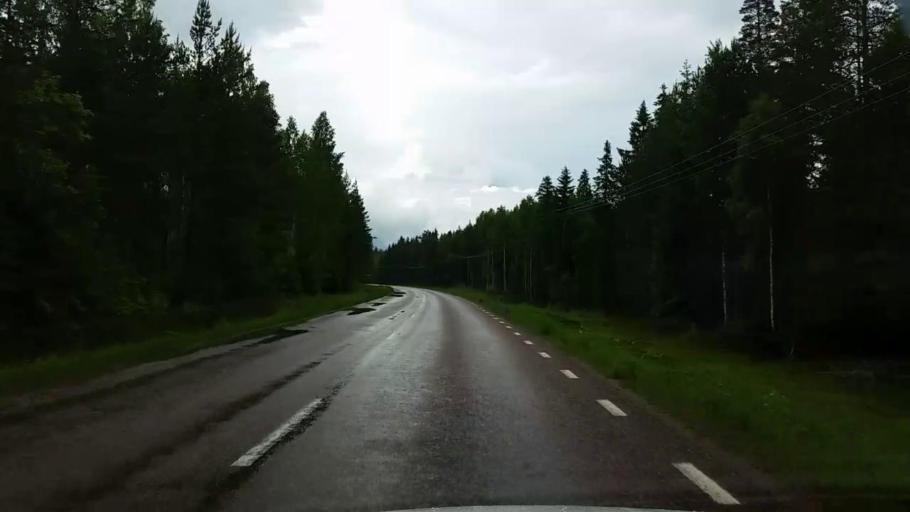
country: SE
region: Gaevleborg
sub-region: Sandvikens Kommun
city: Jarbo
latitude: 60.6684
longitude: 16.6182
